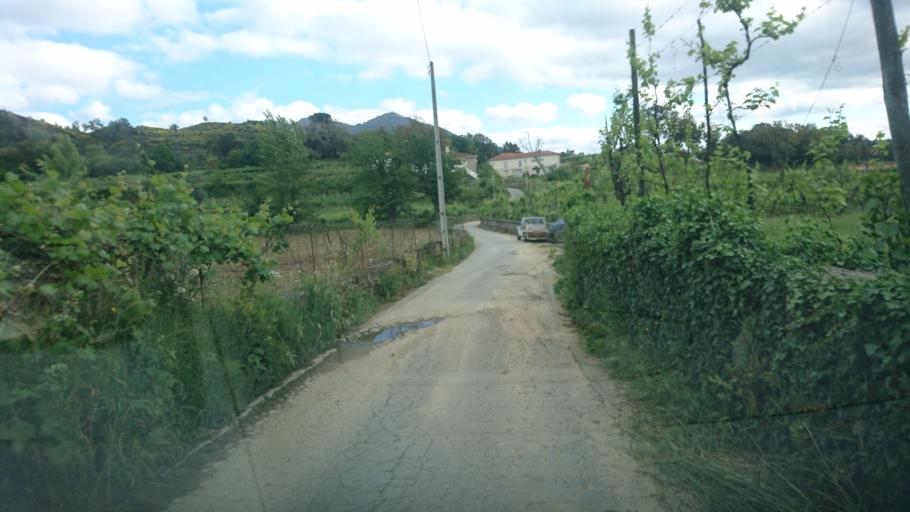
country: PT
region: Vila Real
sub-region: Mondim de Basto
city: Mondim de Basto
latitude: 41.4526
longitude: -7.9281
